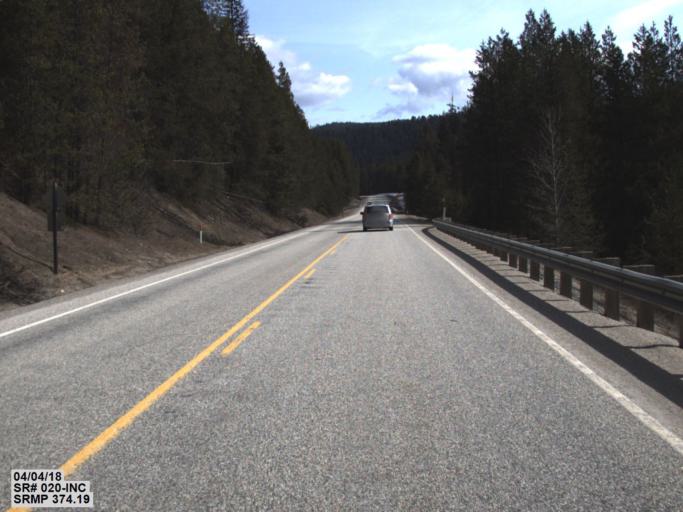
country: US
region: Washington
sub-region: Stevens County
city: Chewelah
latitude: 48.5482
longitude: -117.5728
